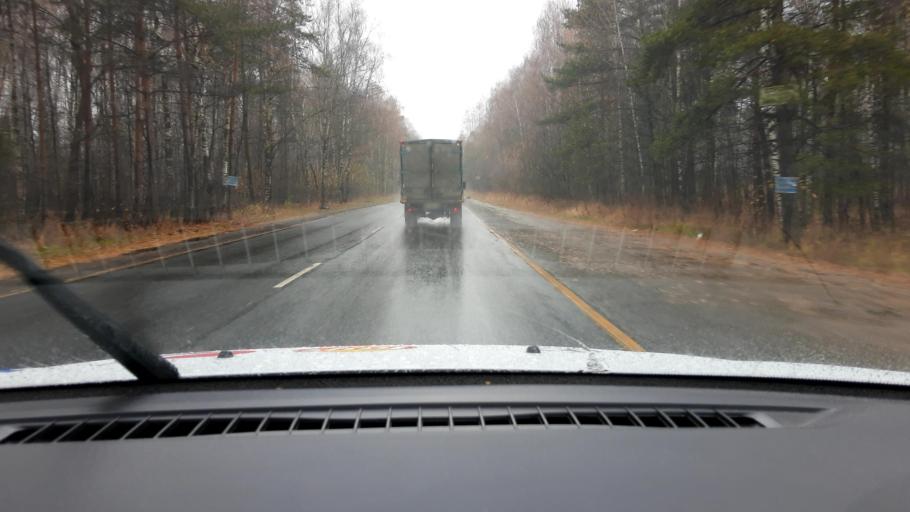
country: RU
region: Nizjnij Novgorod
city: Gorbatovka
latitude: 56.2616
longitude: 43.6909
